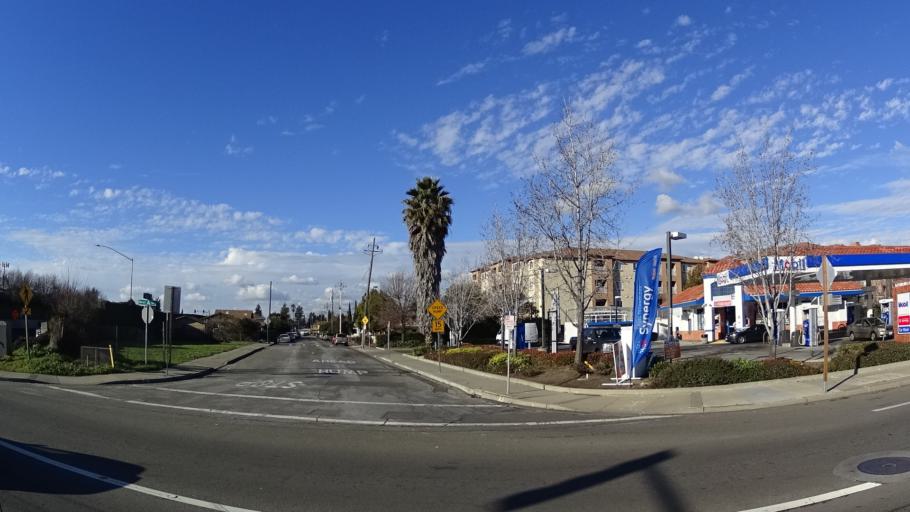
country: US
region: California
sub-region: Alameda County
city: Cherryland
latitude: 37.6663
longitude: -122.1068
